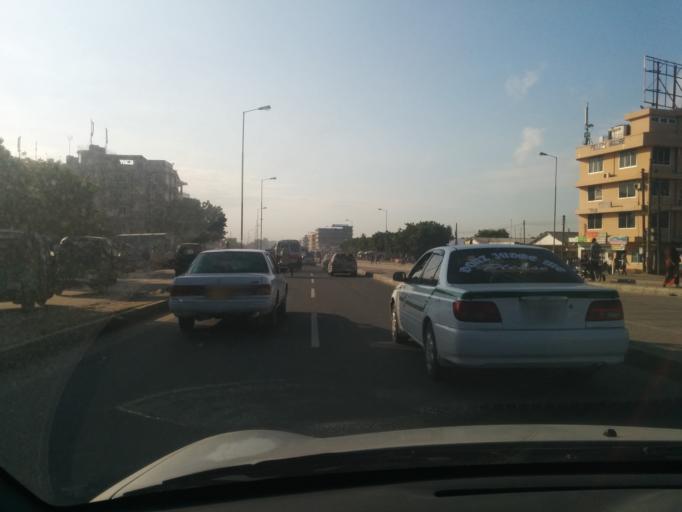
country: TZ
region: Dar es Salaam
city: Magomeni
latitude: -6.7985
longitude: 39.2324
